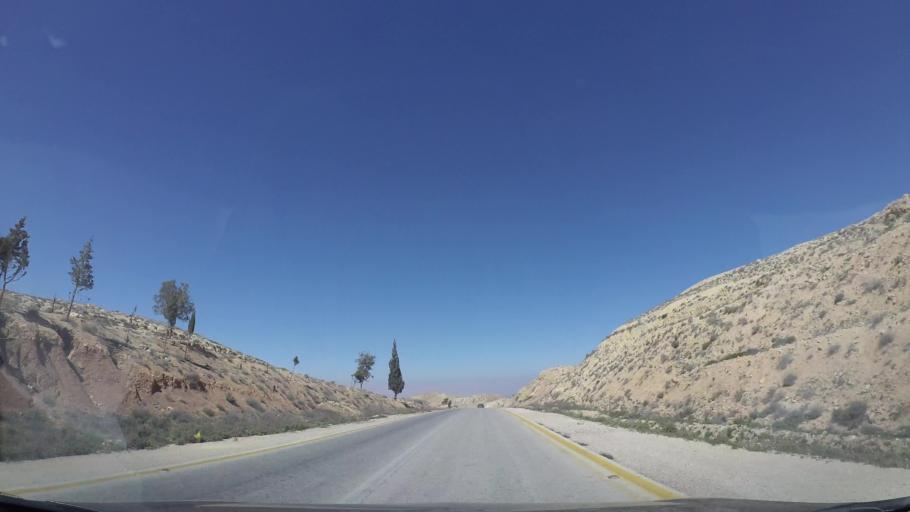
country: JO
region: Tafielah
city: At Tafilah
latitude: 30.8493
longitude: 35.5571
